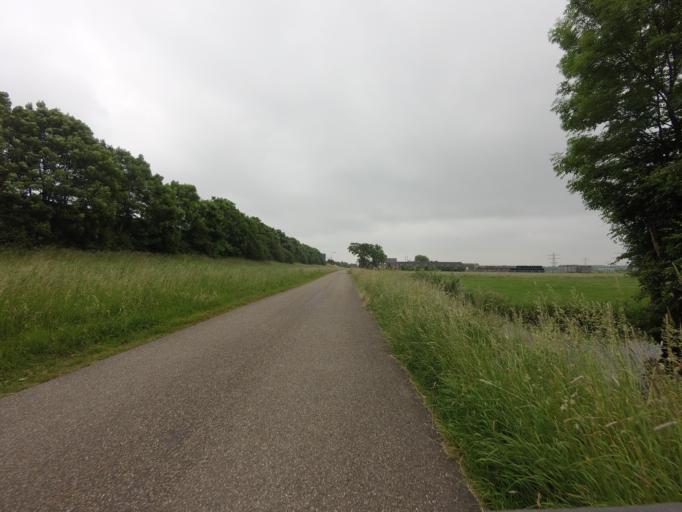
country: NL
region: Utrecht
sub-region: Gemeente IJsselstein
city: IJsselstein
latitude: 52.0695
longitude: 5.0497
